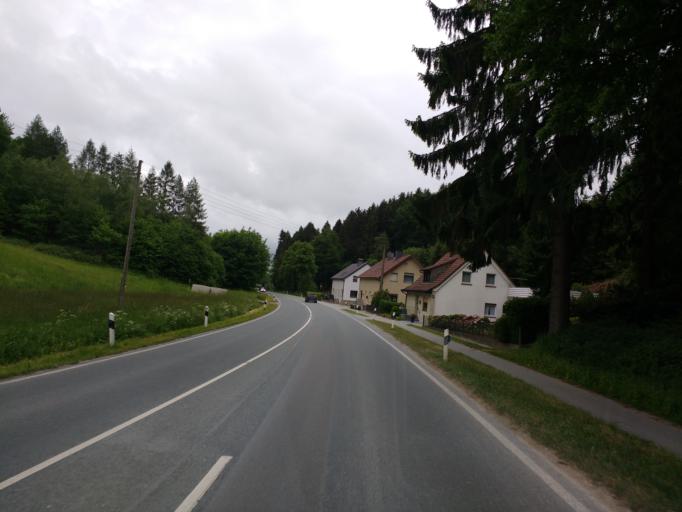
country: DE
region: Lower Saxony
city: Hilter
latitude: 52.1542
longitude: 8.1537
